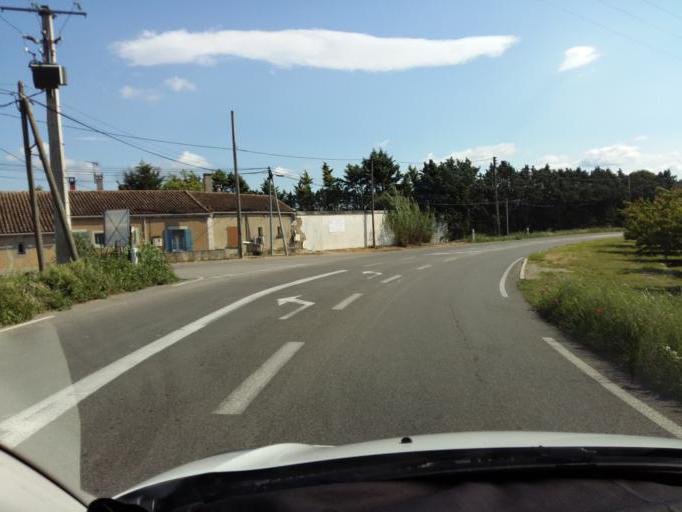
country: FR
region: Provence-Alpes-Cote d'Azur
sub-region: Departement du Vaucluse
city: Cavaillon
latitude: 43.8482
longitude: 5.0604
